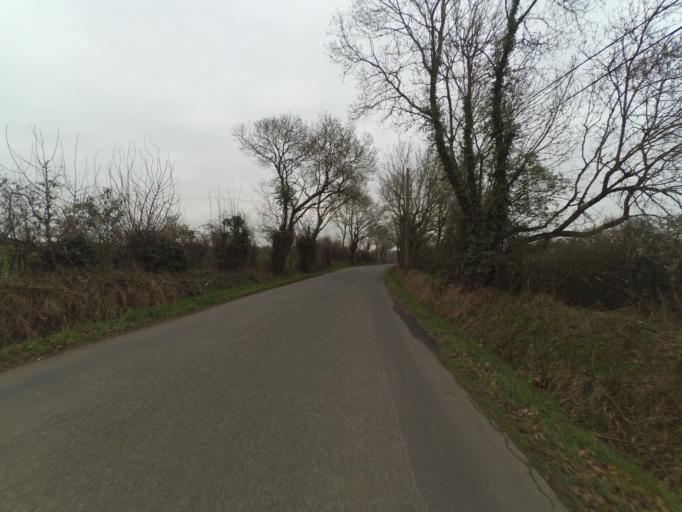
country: FR
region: Pays de la Loire
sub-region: Departement de la Loire-Atlantique
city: Coueron
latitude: 47.2355
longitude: -1.6973
